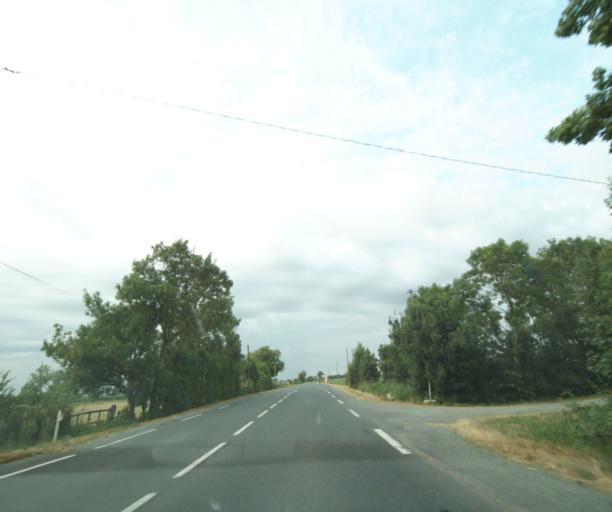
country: FR
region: Poitou-Charentes
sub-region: Departement de la Charente-Maritime
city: Marans
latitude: 46.3505
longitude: -0.9954
